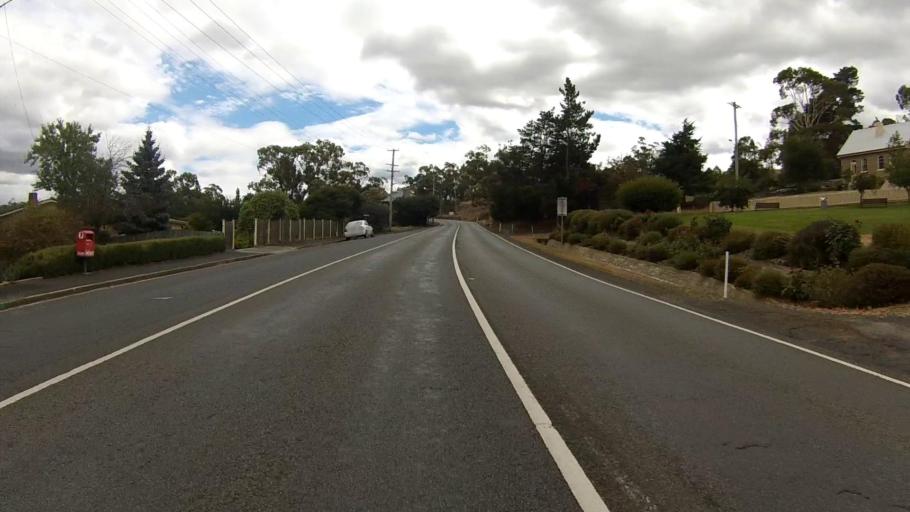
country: AU
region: Tasmania
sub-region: Brighton
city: Bridgewater
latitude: -42.6840
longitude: 147.2658
